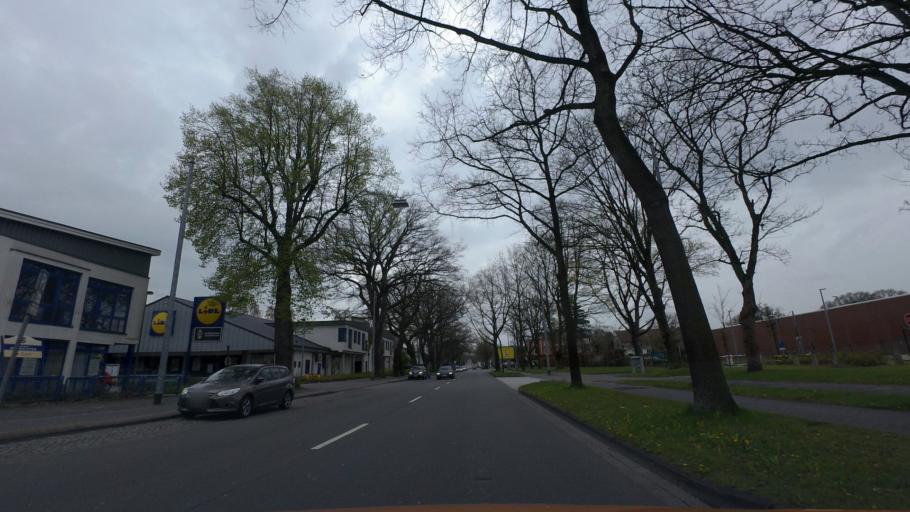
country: DE
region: Lower Saxony
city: Oldenburg
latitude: 53.1081
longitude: 8.2081
